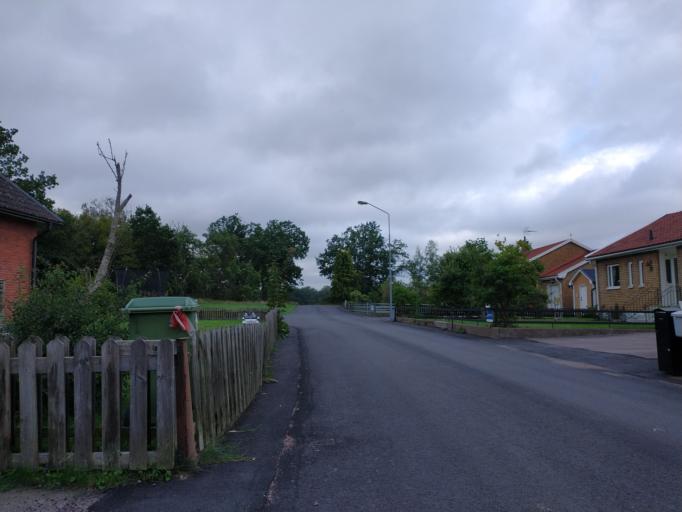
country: SE
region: Kalmar
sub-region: Kalmar Kommun
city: Lindsdal
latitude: 56.7804
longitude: 16.2928
